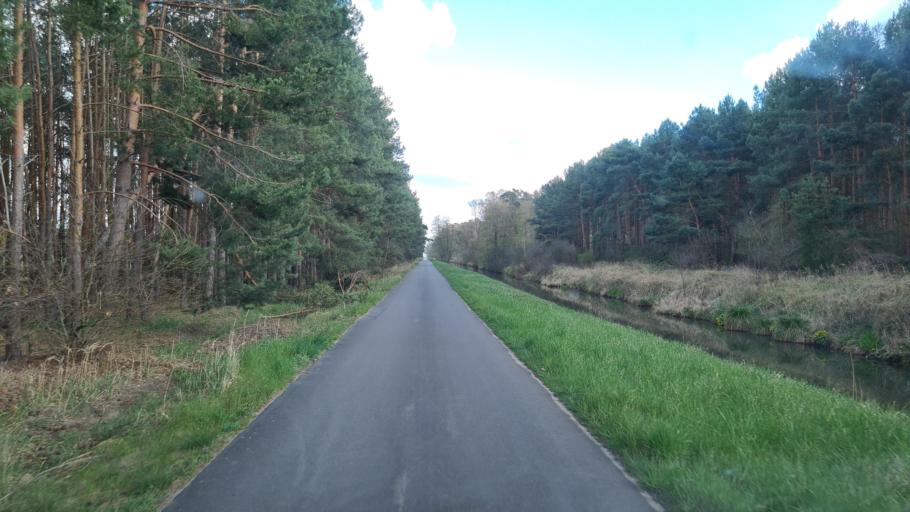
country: DE
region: Brandenburg
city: Herzberg
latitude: 51.7366
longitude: 13.2295
